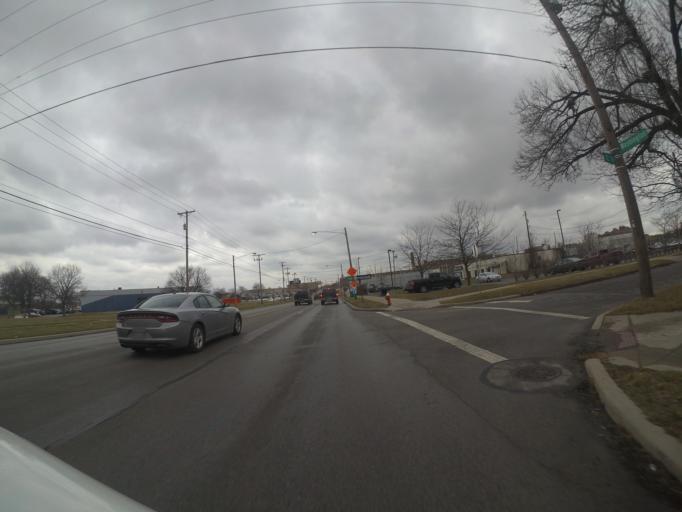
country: US
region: Ohio
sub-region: Lucas County
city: Toledo
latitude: 41.6509
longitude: -83.5454
